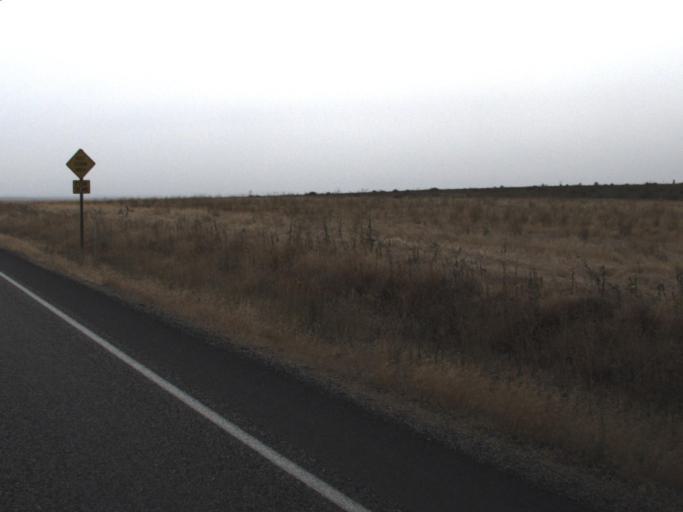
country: US
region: Washington
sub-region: Benton County
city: Benton City
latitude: 46.1809
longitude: -119.6009
